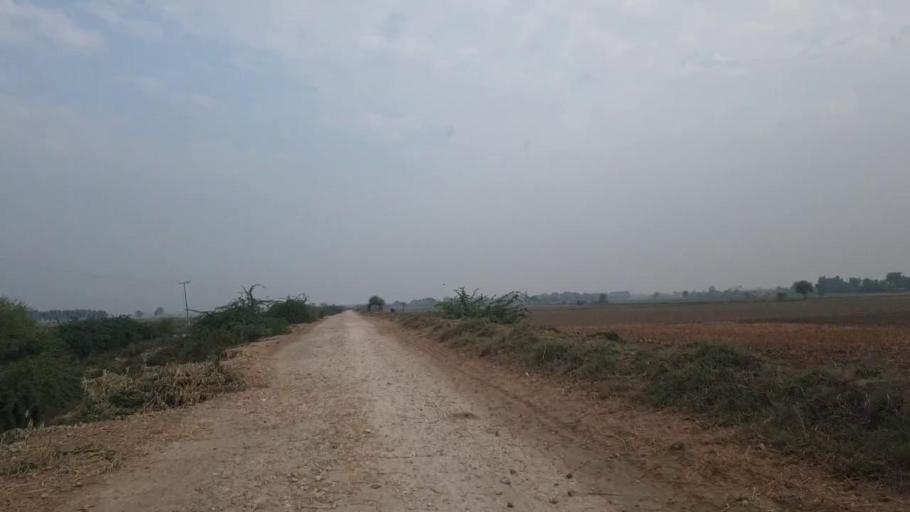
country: PK
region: Sindh
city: Talhar
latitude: 24.8197
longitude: 68.8775
